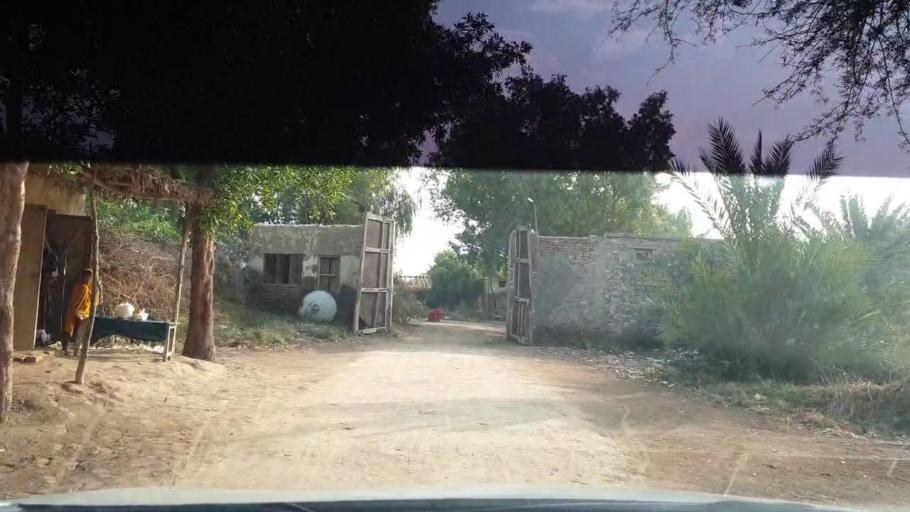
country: PK
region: Sindh
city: Berani
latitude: 25.7596
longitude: 68.9430
